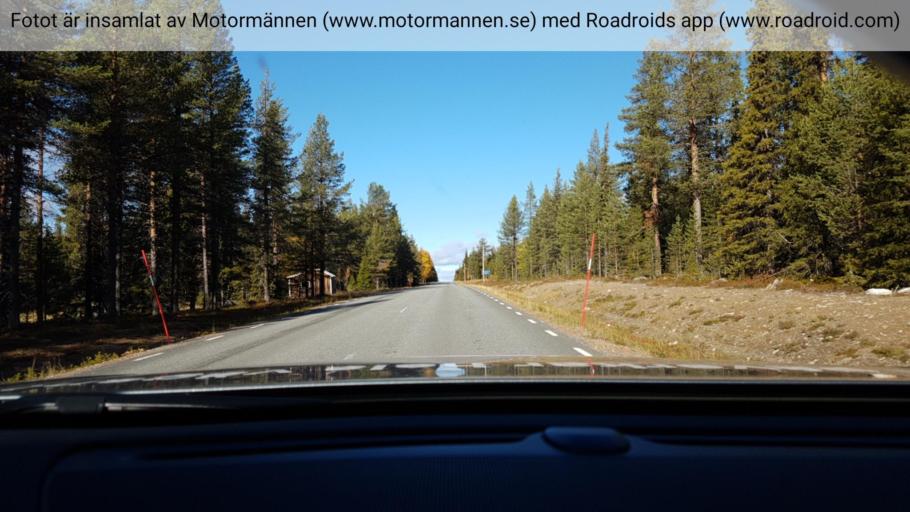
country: SE
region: Vaesterbotten
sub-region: Mala Kommun
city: Mala
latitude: 65.7856
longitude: 18.4949
